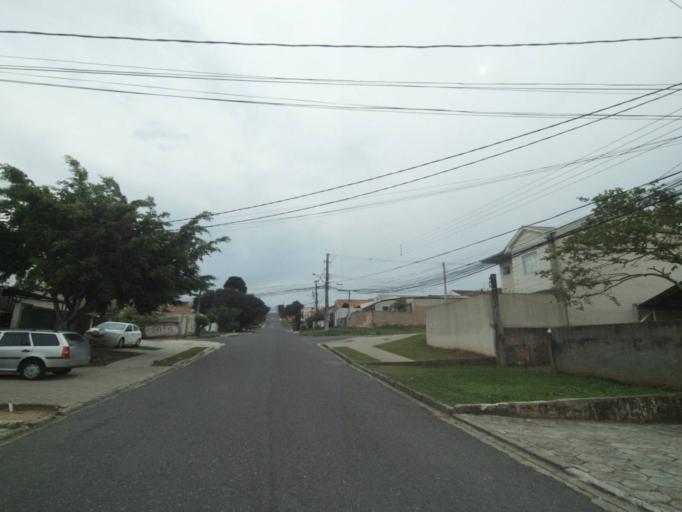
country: BR
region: Parana
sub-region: Pinhais
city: Pinhais
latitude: -25.3975
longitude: -49.2039
